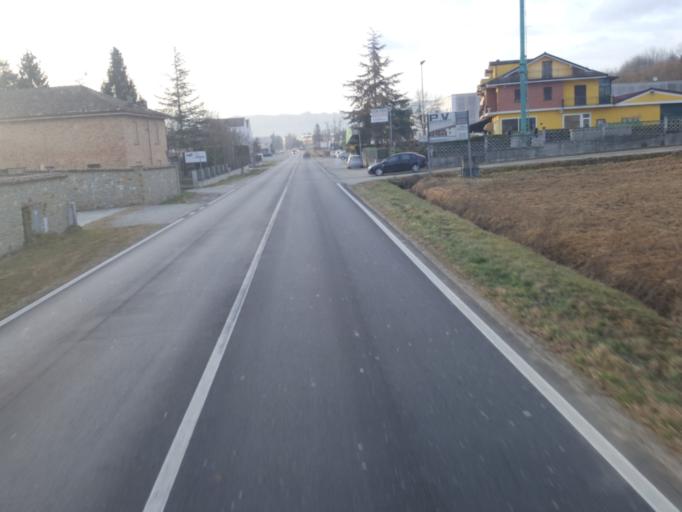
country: IT
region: Piedmont
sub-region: Provincia di Asti
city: San Marzano Oliveto
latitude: 44.7387
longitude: 8.2881
